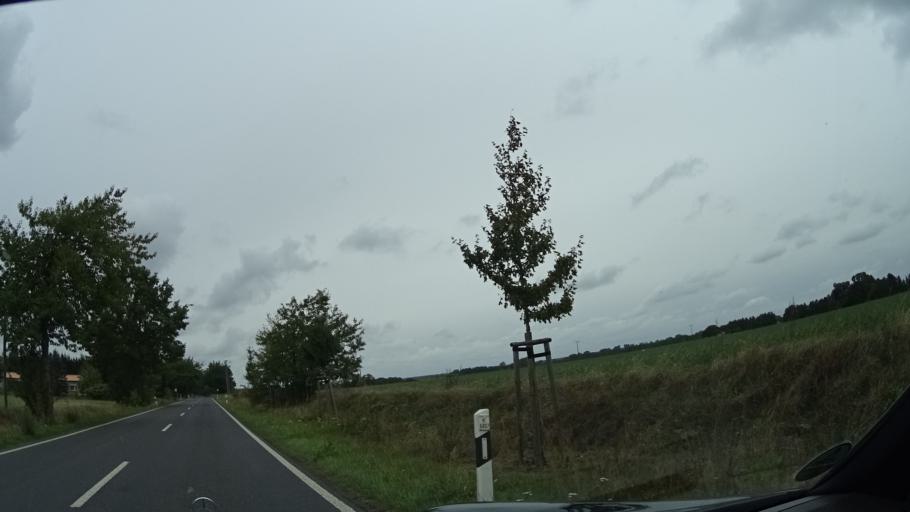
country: DE
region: Brandenburg
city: Dabergotz
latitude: 52.9369
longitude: 12.7288
